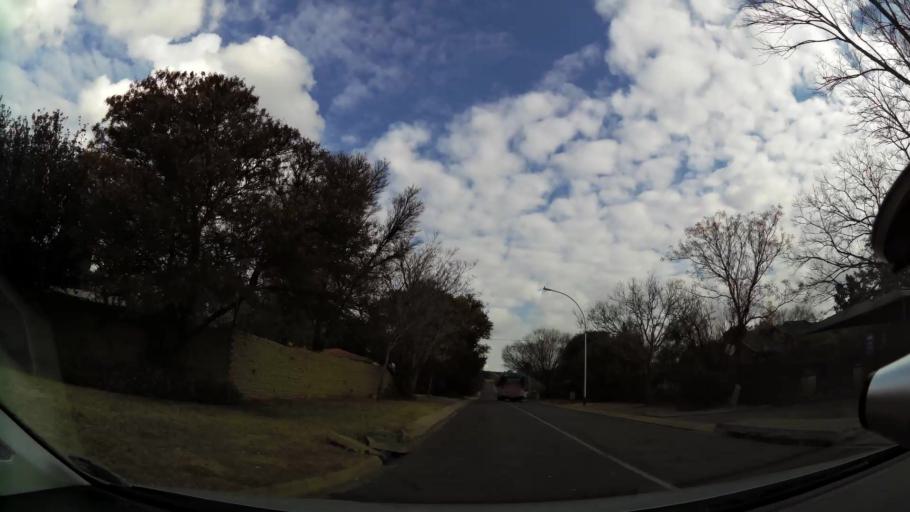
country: ZA
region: Orange Free State
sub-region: Mangaung Metropolitan Municipality
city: Bloemfontein
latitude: -29.0717
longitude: 26.2092
